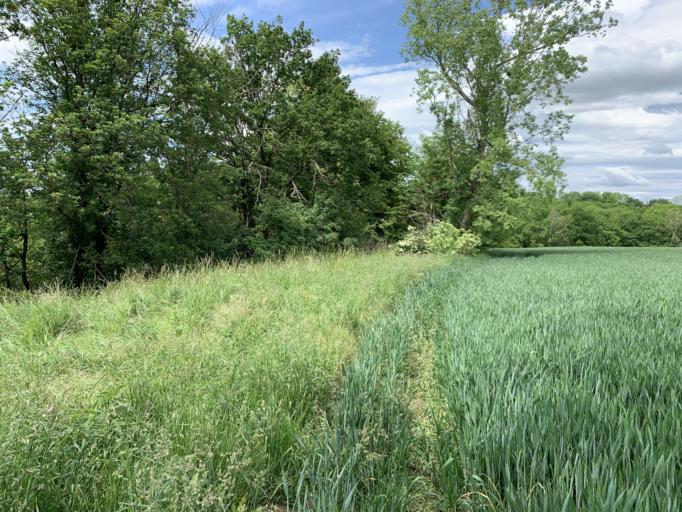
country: DE
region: Saxony
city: Seelitz
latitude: 51.0189
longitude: 12.8401
